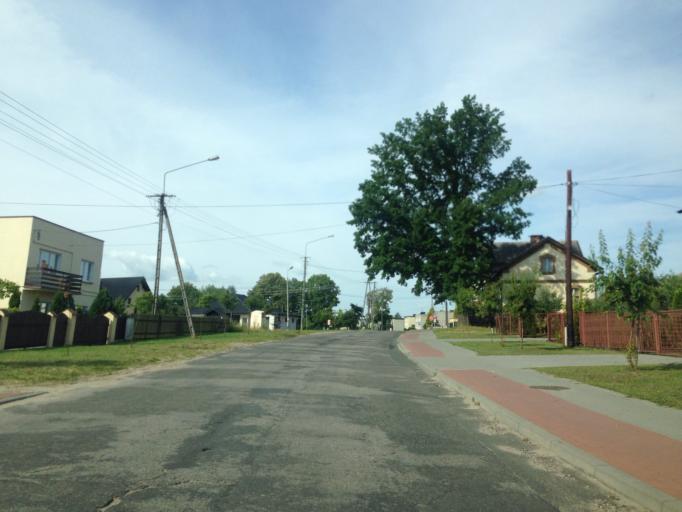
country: PL
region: Kujawsko-Pomorskie
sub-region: Powiat tucholski
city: Sliwice
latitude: 53.7151
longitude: 18.1837
